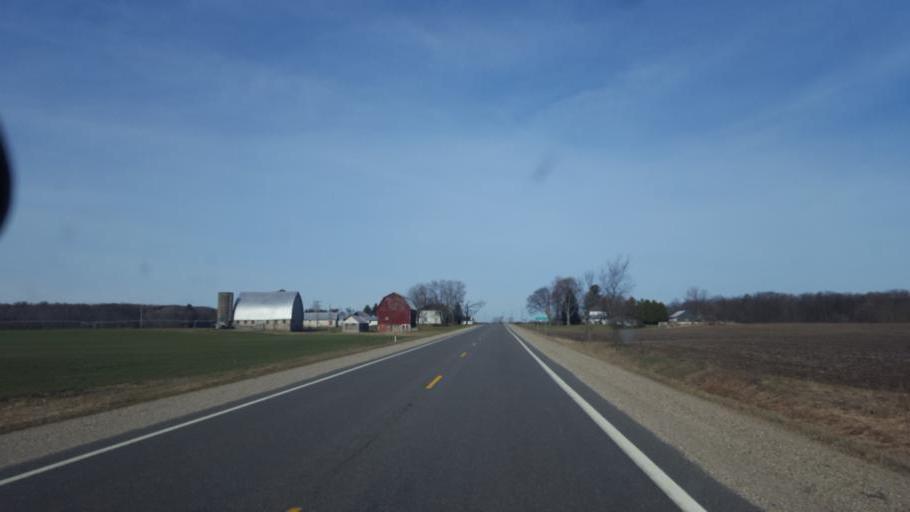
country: US
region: Michigan
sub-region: Montcalm County
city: Lakeview
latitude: 43.4328
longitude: -85.3582
